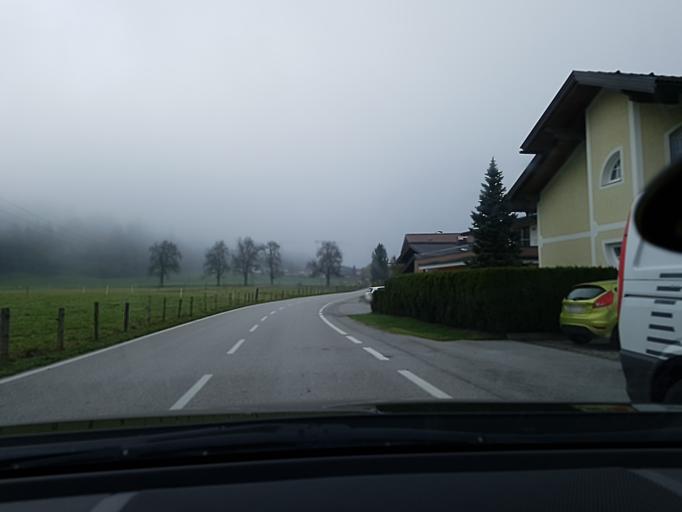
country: AT
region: Salzburg
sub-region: Politischer Bezirk Sankt Johann im Pongau
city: Sankt Johann im Pongau
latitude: 47.3637
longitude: 13.2091
